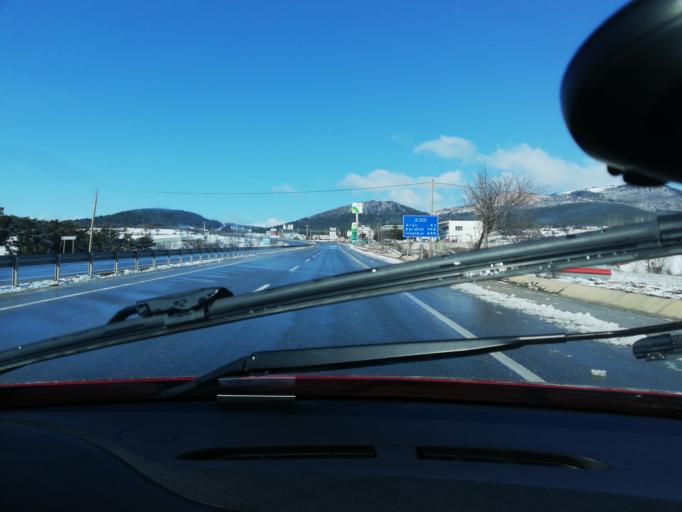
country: TR
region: Kastamonu
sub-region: Cide
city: Kastamonu
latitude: 41.3629
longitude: 33.7197
